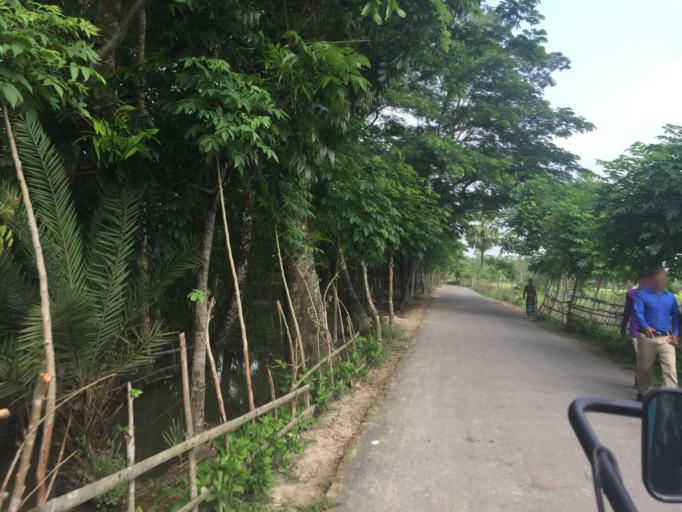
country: BD
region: Barisal
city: Mathba
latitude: 22.2090
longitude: 89.9359
